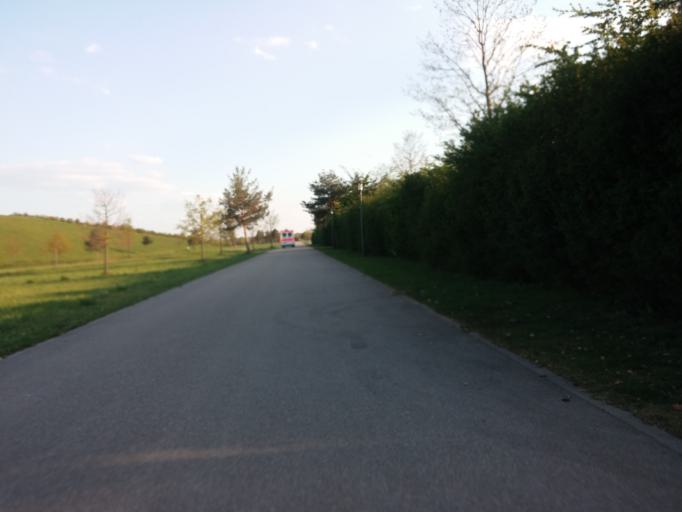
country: DE
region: Bavaria
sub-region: Upper Bavaria
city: Feldkirchen
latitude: 48.1328
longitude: 11.7087
